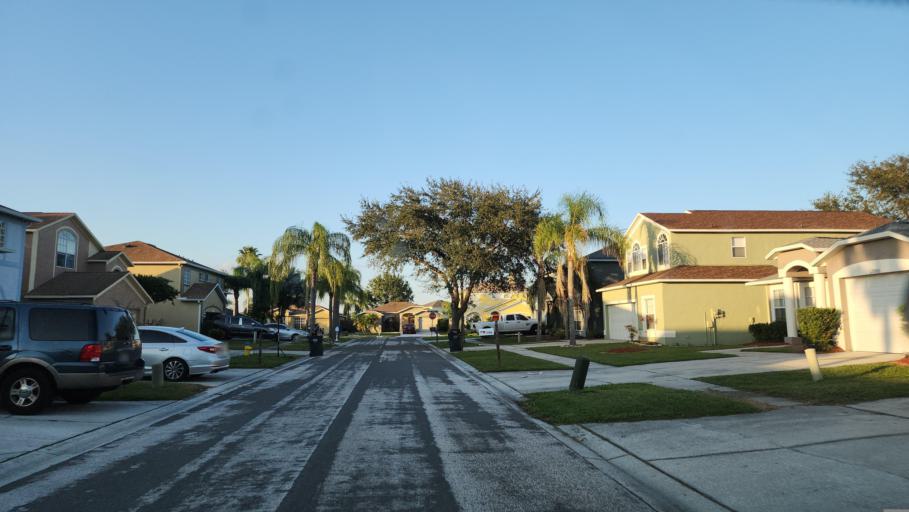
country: US
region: Florida
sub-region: Hillsborough County
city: Balm
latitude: 27.8055
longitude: -82.3051
